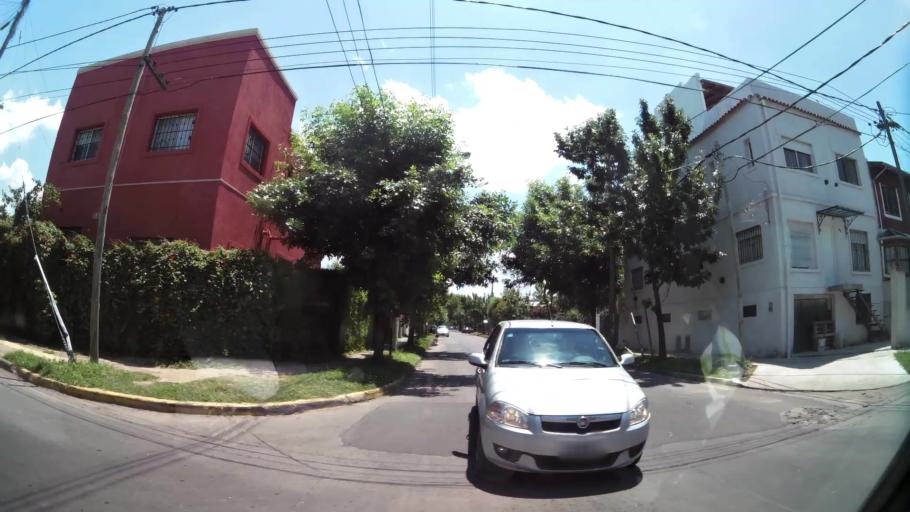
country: AR
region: Buenos Aires
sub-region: Partido de Tigre
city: Tigre
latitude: -34.4216
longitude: -58.5901
